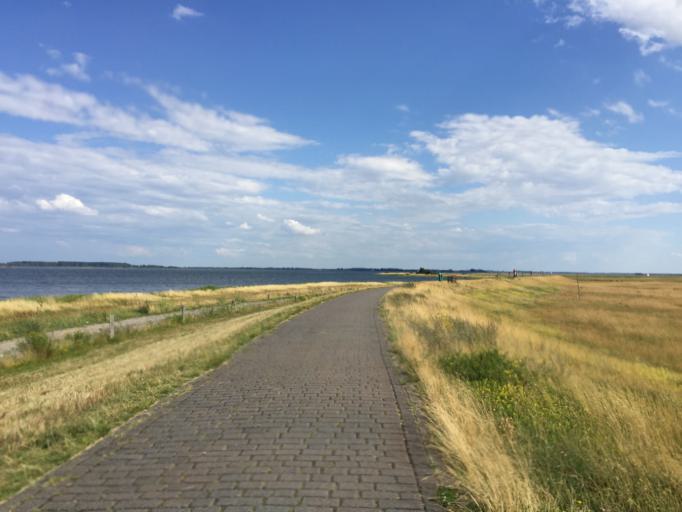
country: DE
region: Mecklenburg-Vorpommern
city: Hiddensee
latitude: 54.5808
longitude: 13.1105
